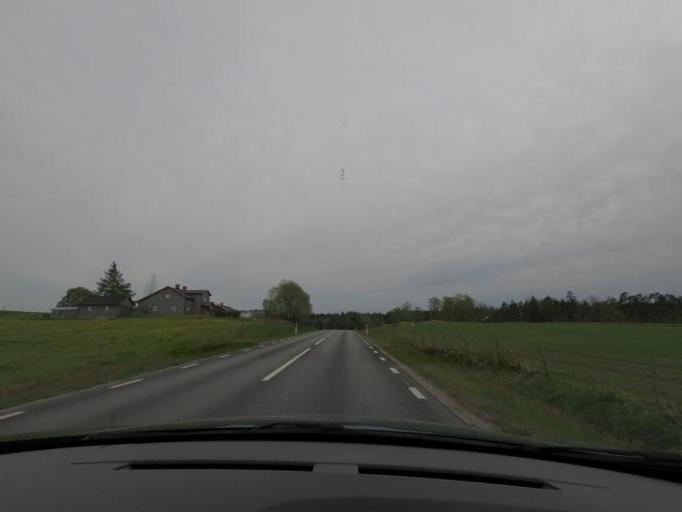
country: SE
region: Joenkoeping
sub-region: Varnamo Kommun
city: Bredaryd
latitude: 57.2010
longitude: 13.7625
